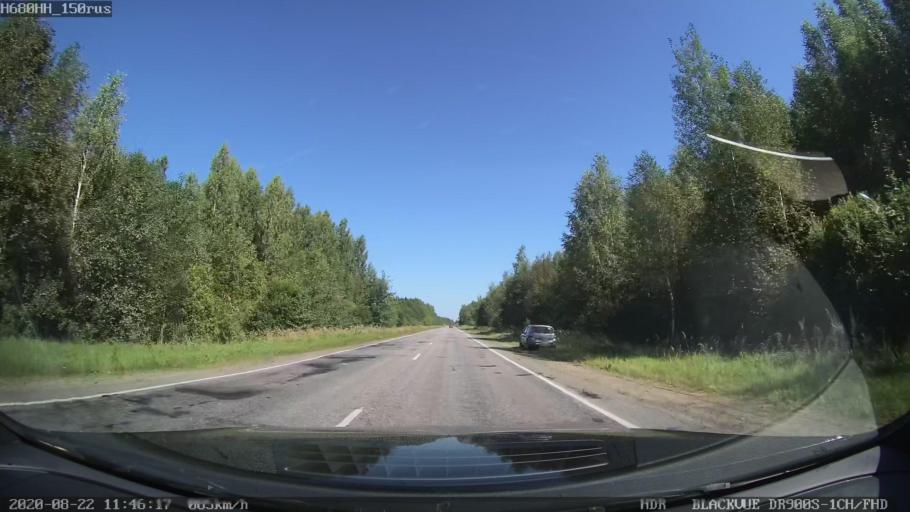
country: RU
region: Tverskaya
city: Sakharovo
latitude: 57.0403
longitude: 36.0729
